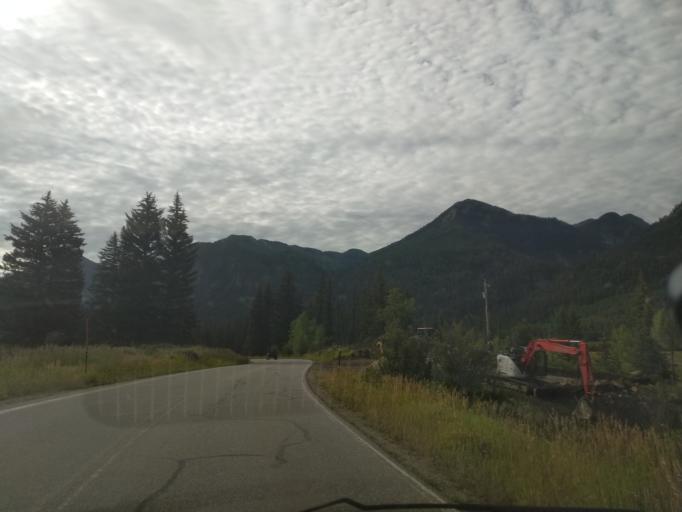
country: US
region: Colorado
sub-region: Gunnison County
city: Crested Butte
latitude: 39.0797
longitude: -107.2291
